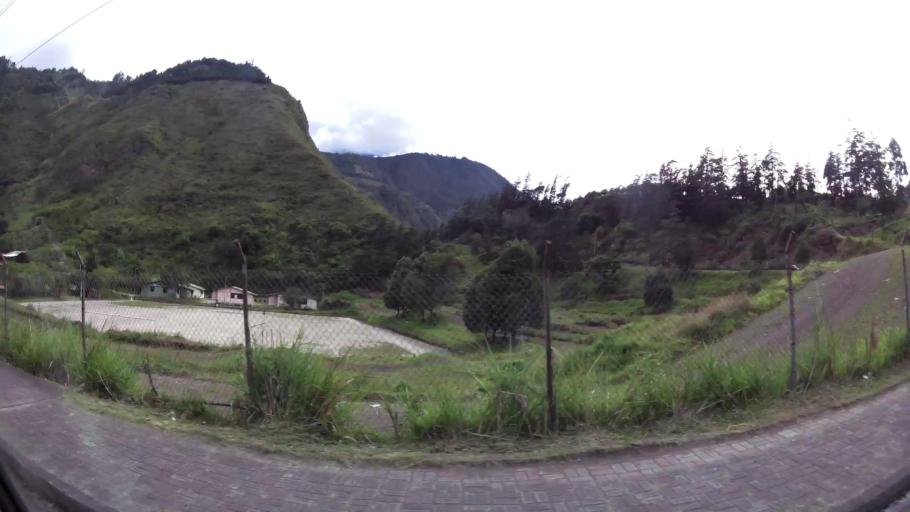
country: EC
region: Tungurahua
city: Banos
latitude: -1.3924
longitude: -78.4145
